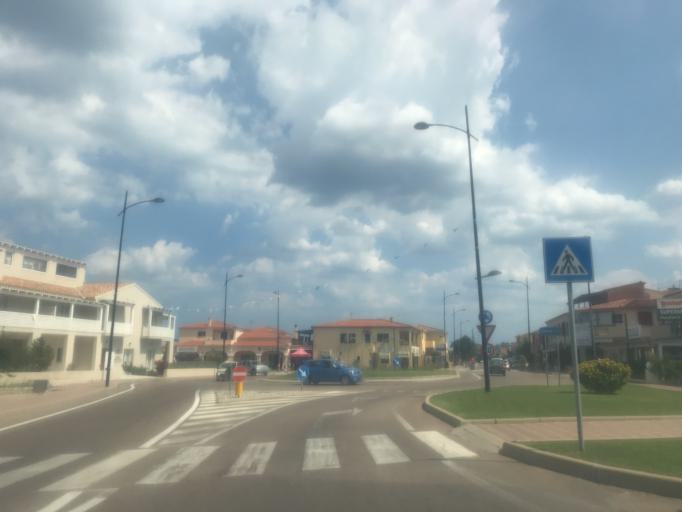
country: IT
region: Sardinia
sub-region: Provincia di Olbia-Tempio
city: Golfo Arnaci
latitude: 40.8760
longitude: 9.6284
